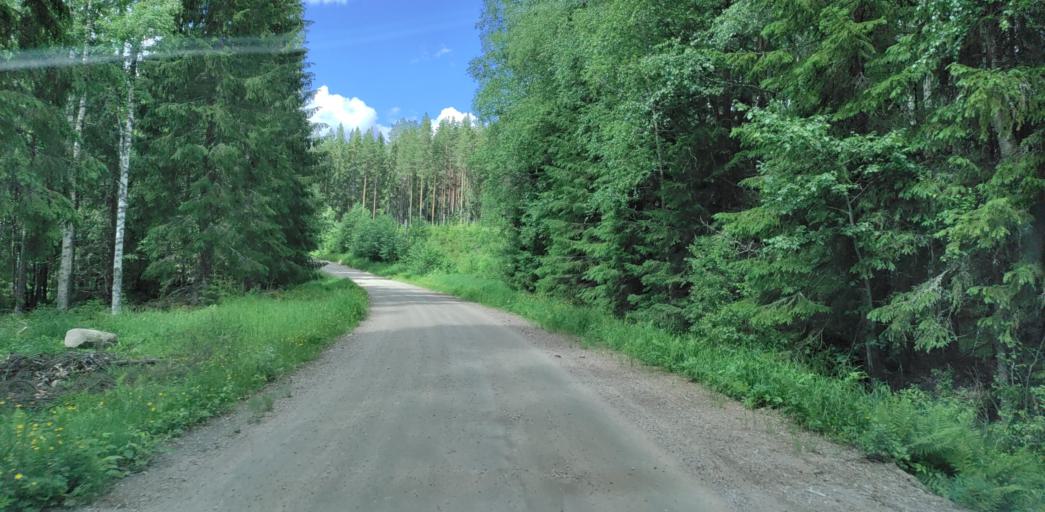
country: SE
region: Vaermland
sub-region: Hagfors Kommun
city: Ekshaerad
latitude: 60.0968
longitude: 13.4008
